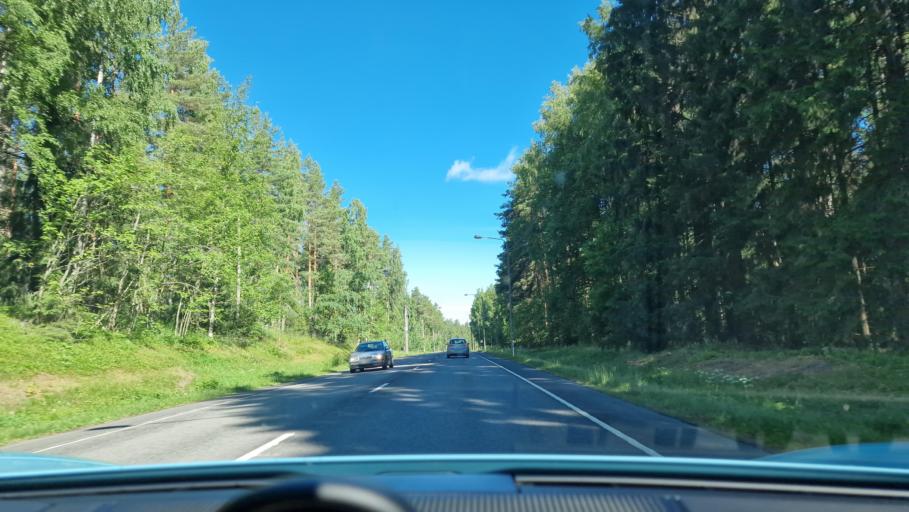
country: FI
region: Pirkanmaa
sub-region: Tampere
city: Kangasala
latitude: 61.4276
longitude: 24.1331
